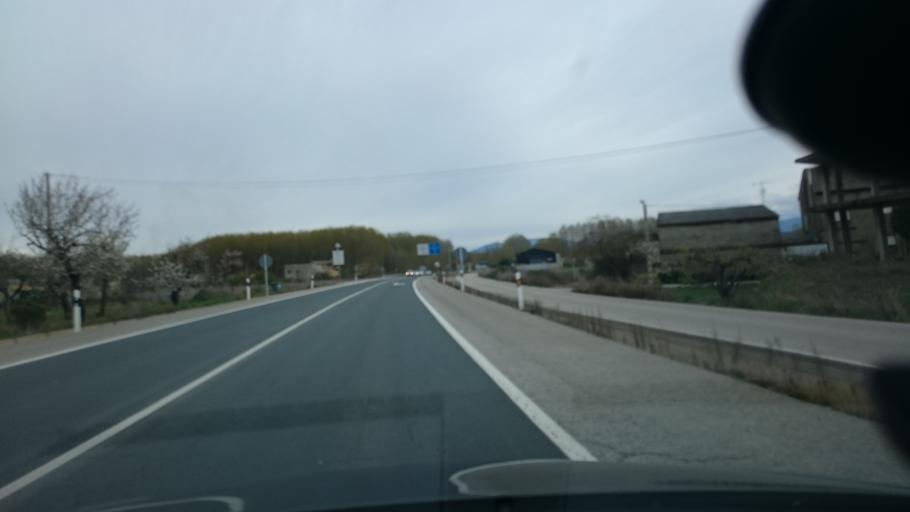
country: ES
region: Castille and Leon
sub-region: Provincia de Leon
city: Villadecanes
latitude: 42.5686
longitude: -6.7495
